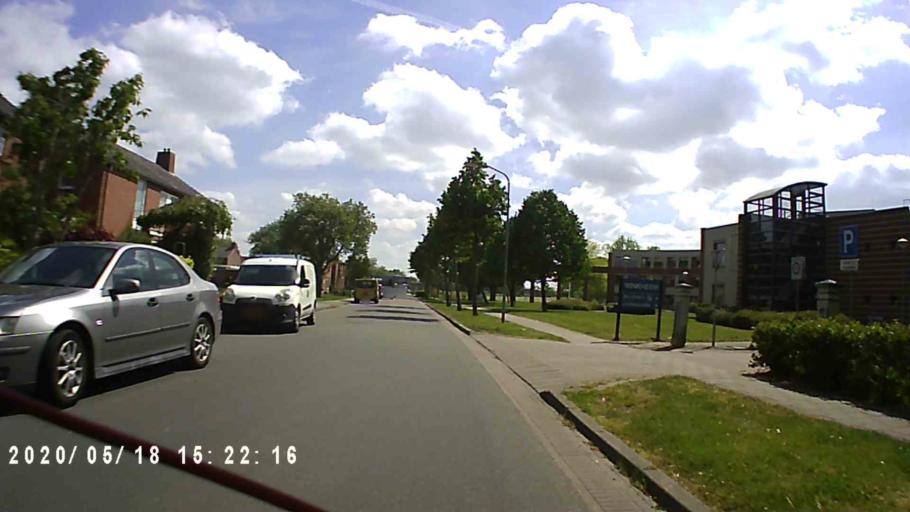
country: NL
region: Groningen
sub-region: Gemeente Winsum
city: Winsum
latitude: 53.3278
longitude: 6.5193
